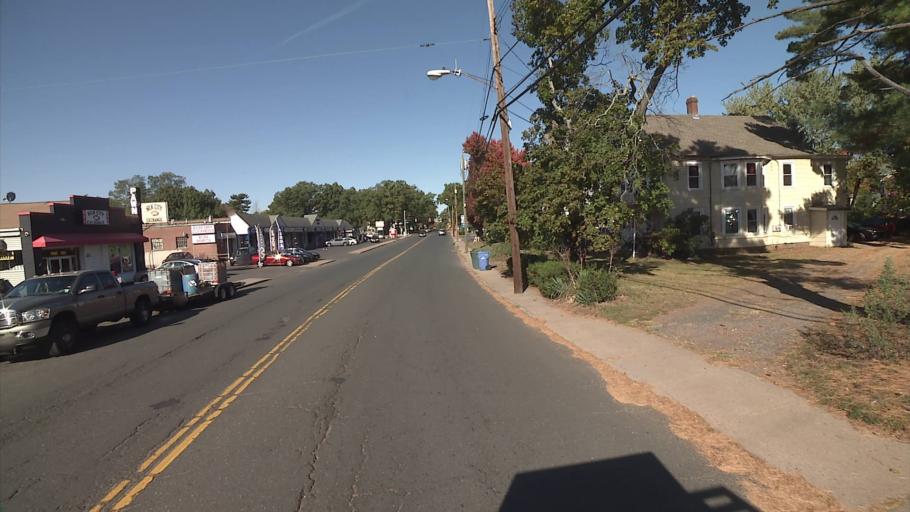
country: US
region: Connecticut
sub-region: Hartford County
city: Manchester
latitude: 41.7745
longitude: -72.5474
